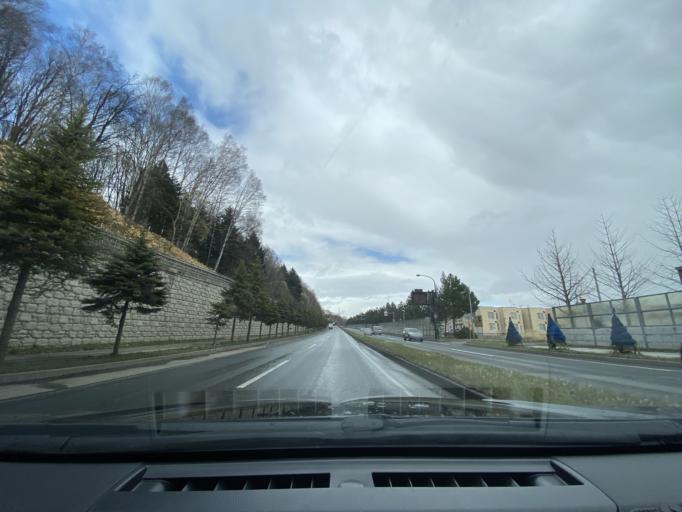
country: JP
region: Hokkaido
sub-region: Asahikawa-shi
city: Asahikawa
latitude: 43.8092
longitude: 142.3601
